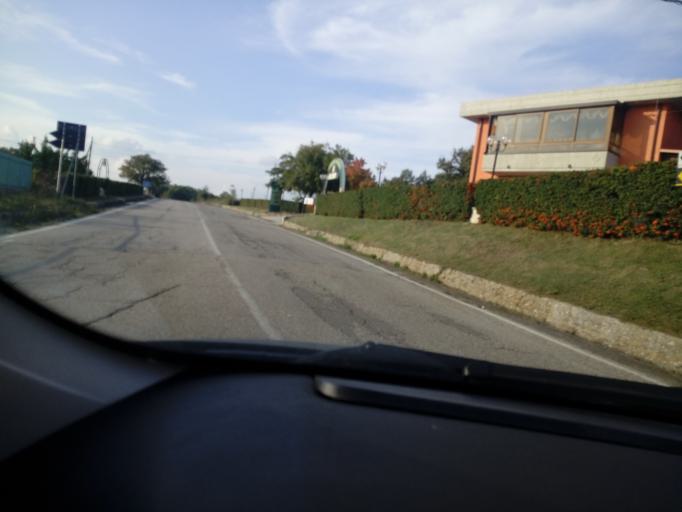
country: IT
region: Molise
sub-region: Provincia di Campobasso
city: Jelsi
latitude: 41.5108
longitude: 14.8239
